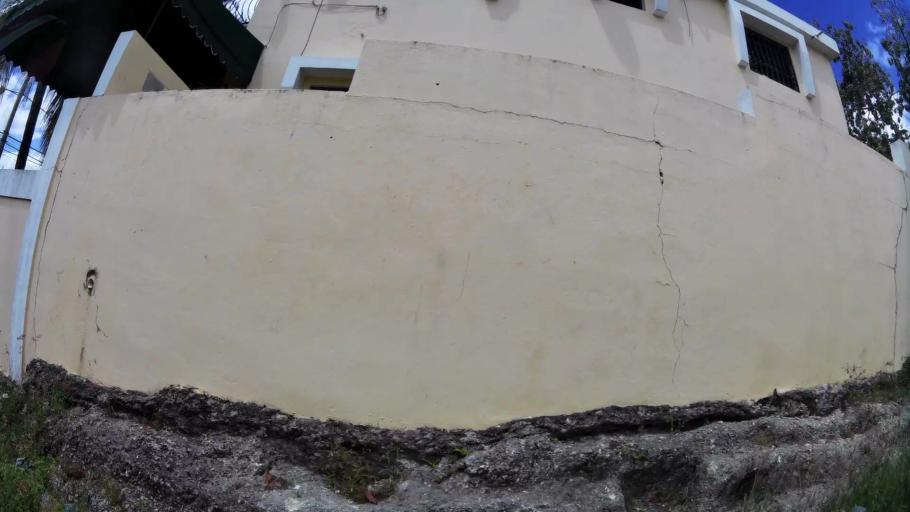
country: DO
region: Nacional
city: Ensanche Luperon
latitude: 18.5252
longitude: -69.9087
